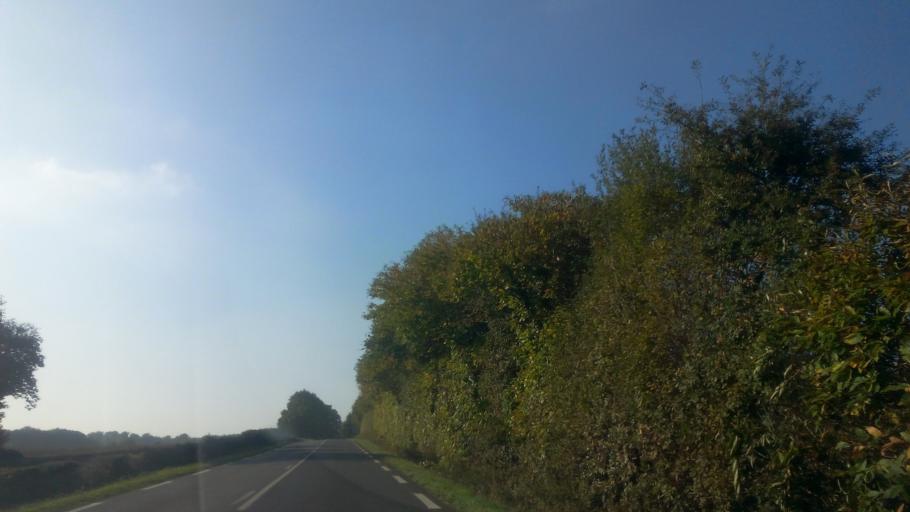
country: FR
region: Pays de la Loire
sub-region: Departement de la Loire-Atlantique
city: Avessac
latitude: 47.6396
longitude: -2.0024
